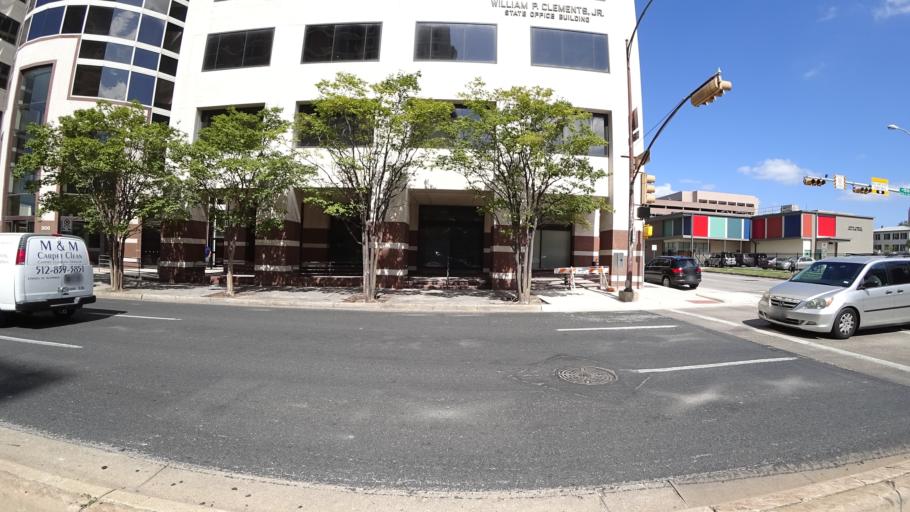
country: US
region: Texas
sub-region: Travis County
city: Austin
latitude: 30.2777
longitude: -97.7421
